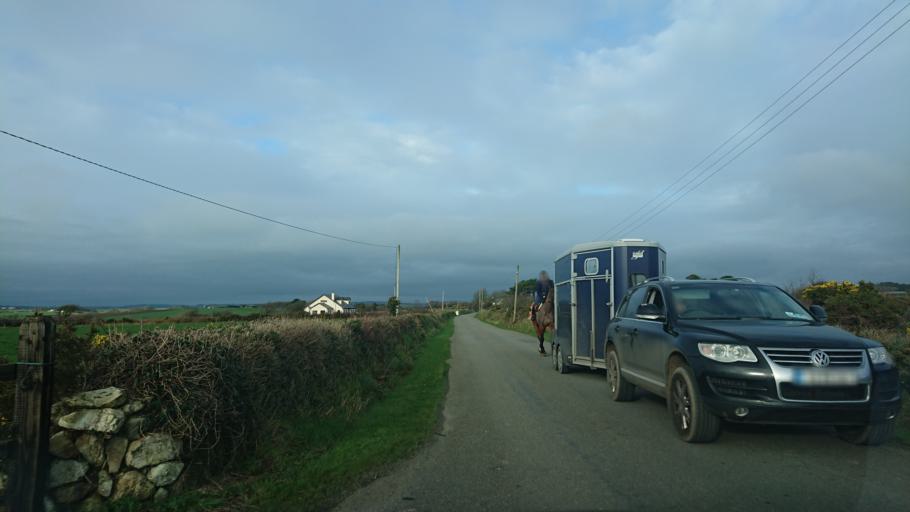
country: IE
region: Munster
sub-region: Waterford
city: Tra Mhor
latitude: 52.1532
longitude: -7.2139
